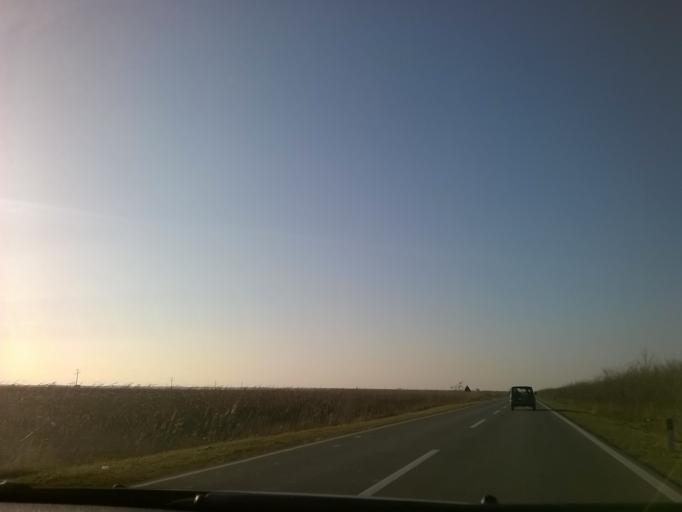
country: RS
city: Uljma
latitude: 45.0492
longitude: 21.1118
